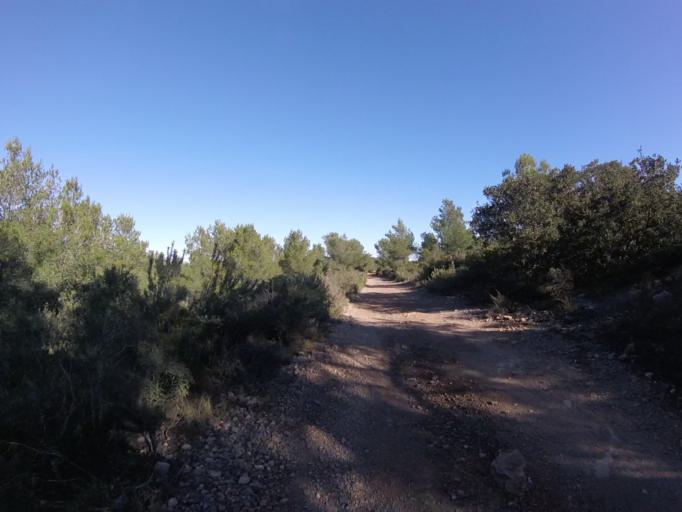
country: ES
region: Valencia
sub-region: Provincia de Castello
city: Orpesa/Oropesa del Mar
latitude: 40.0914
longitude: 0.1042
